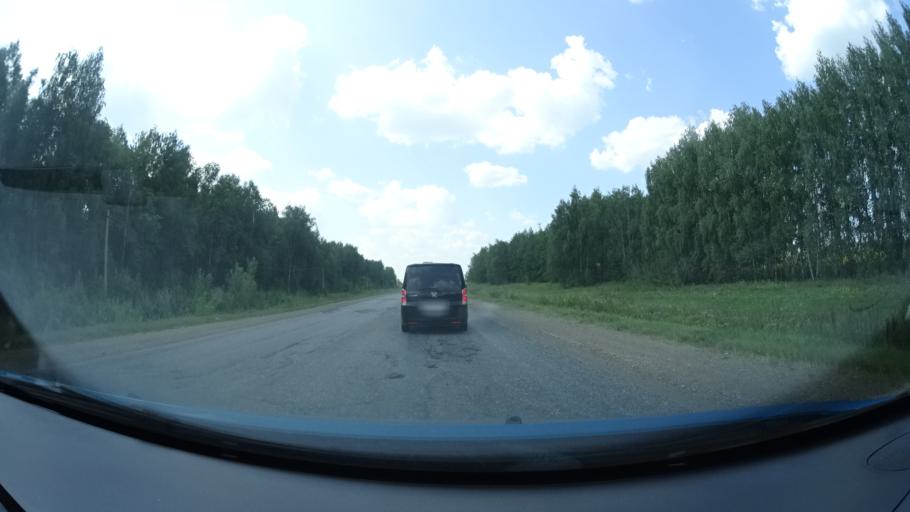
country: RU
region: Bashkortostan
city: Buzdyak
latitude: 54.6846
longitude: 54.8093
